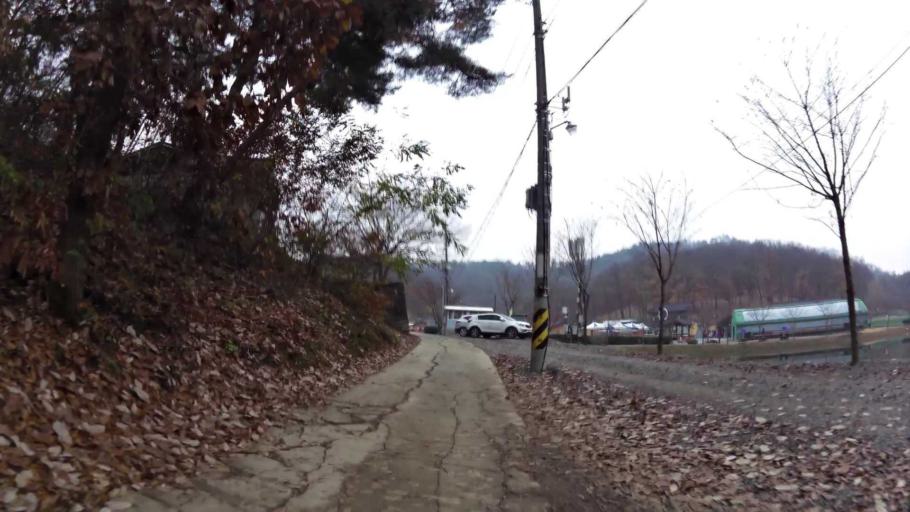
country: KR
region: Daegu
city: Daegu
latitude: 35.8596
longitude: 128.6621
